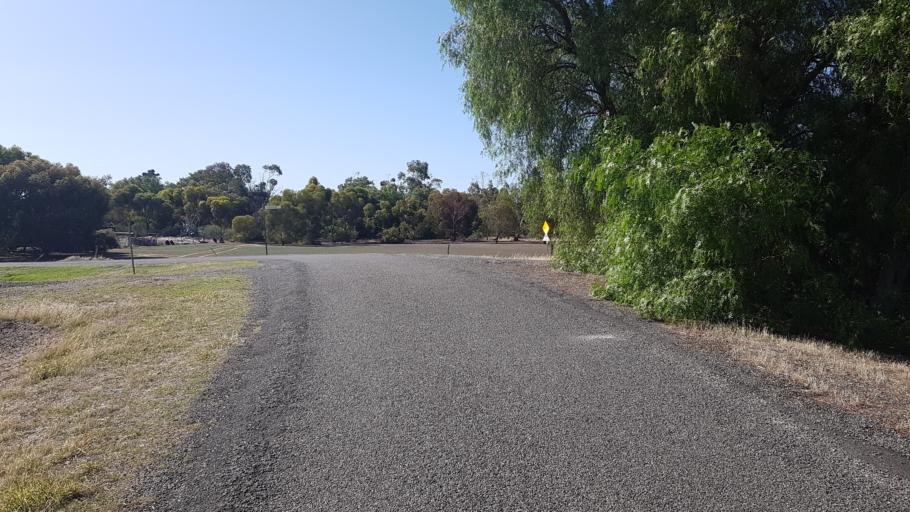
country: AU
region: Victoria
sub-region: Horsham
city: Horsham
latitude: -36.7440
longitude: 141.9429
